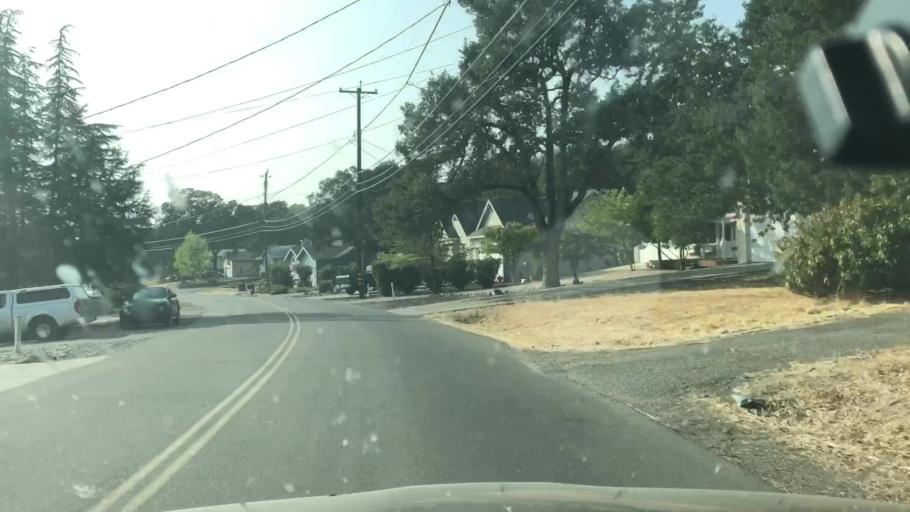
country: US
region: California
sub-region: Lake County
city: Hidden Valley Lake
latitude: 38.8020
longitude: -122.5574
